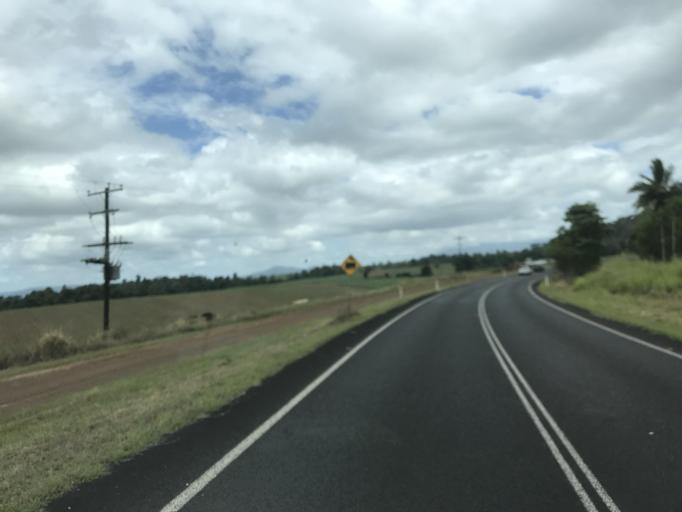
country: AU
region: Queensland
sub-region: Cassowary Coast
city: Innisfail
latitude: -17.5764
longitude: 145.9614
